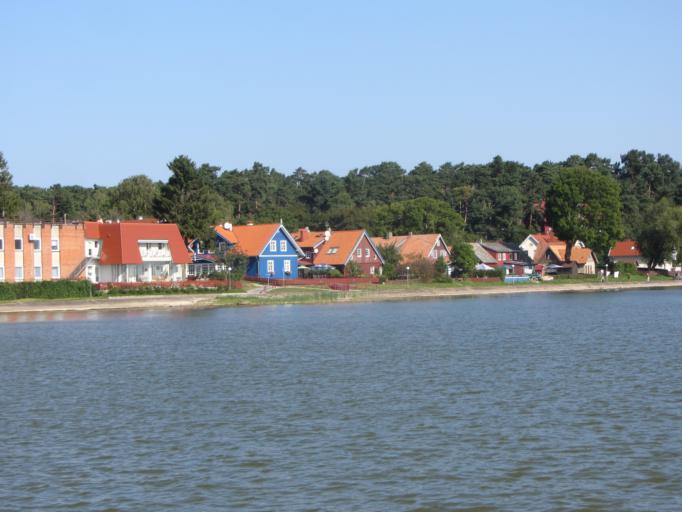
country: LT
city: Nida
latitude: 55.3091
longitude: 21.0115
